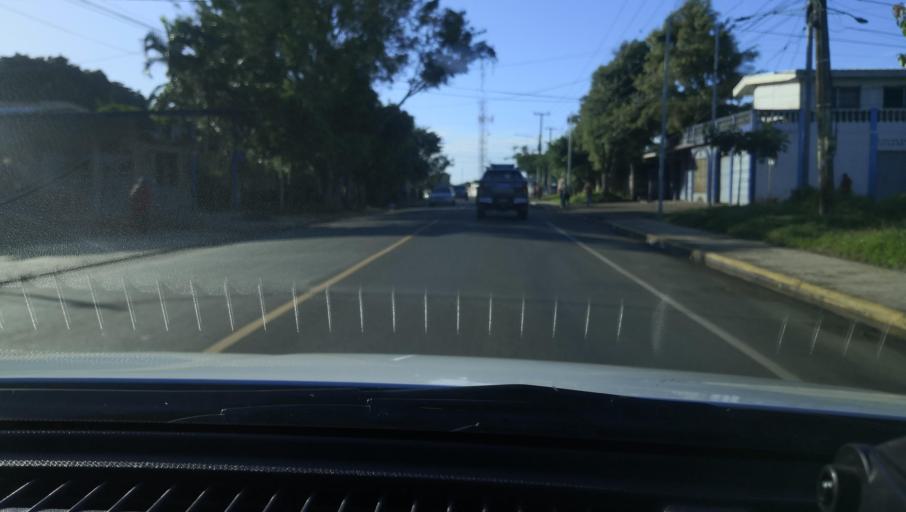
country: NI
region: Carazo
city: Jinotepe
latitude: 11.8526
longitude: -86.2056
